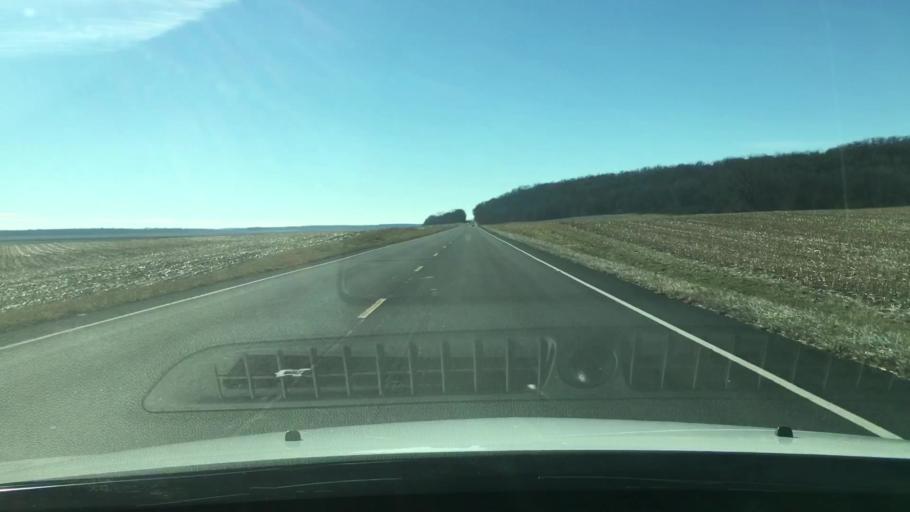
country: US
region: Illinois
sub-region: Fulton County
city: Canton
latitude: 40.4421
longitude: -89.9661
